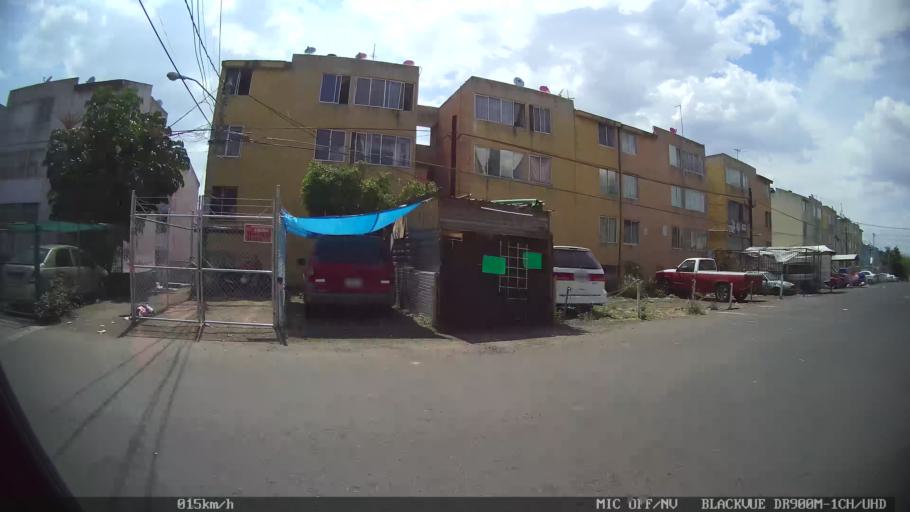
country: MX
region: Jalisco
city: Tonala
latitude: 20.6227
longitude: -103.2518
